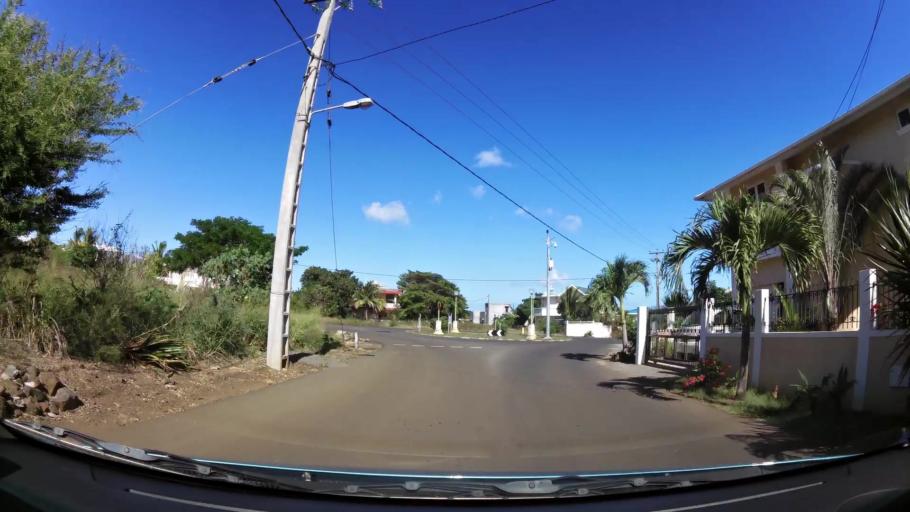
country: MU
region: Black River
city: Flic en Flac
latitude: -20.2729
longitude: 57.3750
